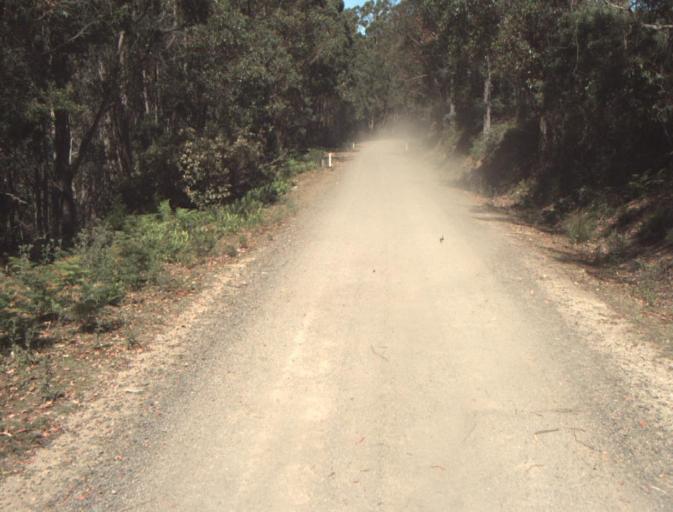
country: AU
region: Tasmania
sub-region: Dorset
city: Scottsdale
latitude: -41.3794
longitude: 147.4933
